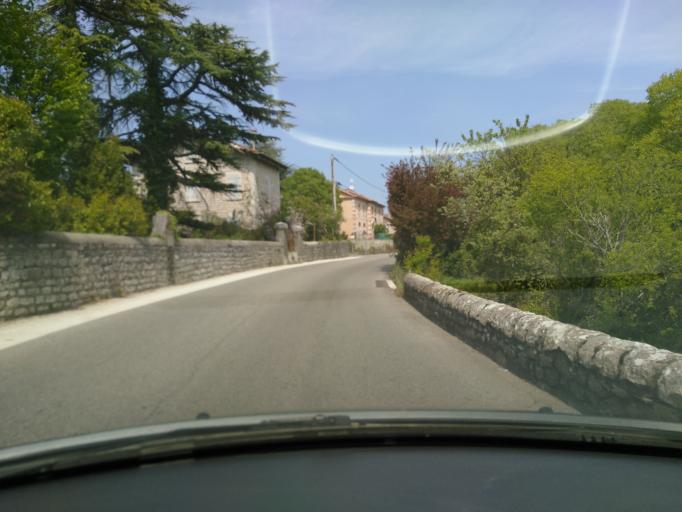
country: FR
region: Rhone-Alpes
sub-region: Departement de l'Ardeche
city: Saint-Sernin
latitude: 44.5406
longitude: 4.4149
